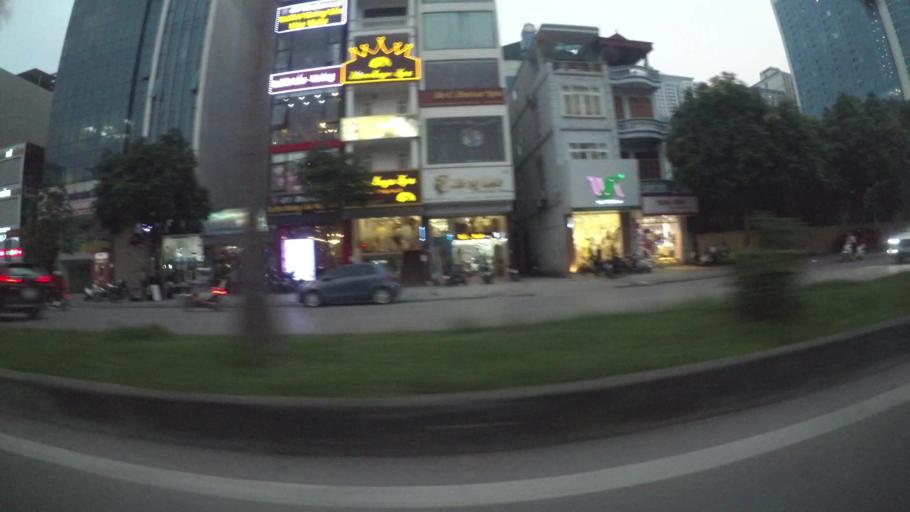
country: VN
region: Ha Noi
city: Ha Dong
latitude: 20.9784
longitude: 105.7874
